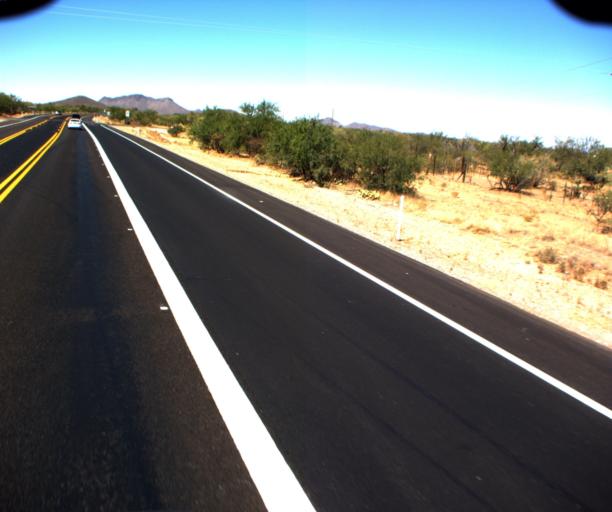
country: US
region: Arizona
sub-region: Pima County
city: Sells
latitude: 31.9356
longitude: -111.7760
